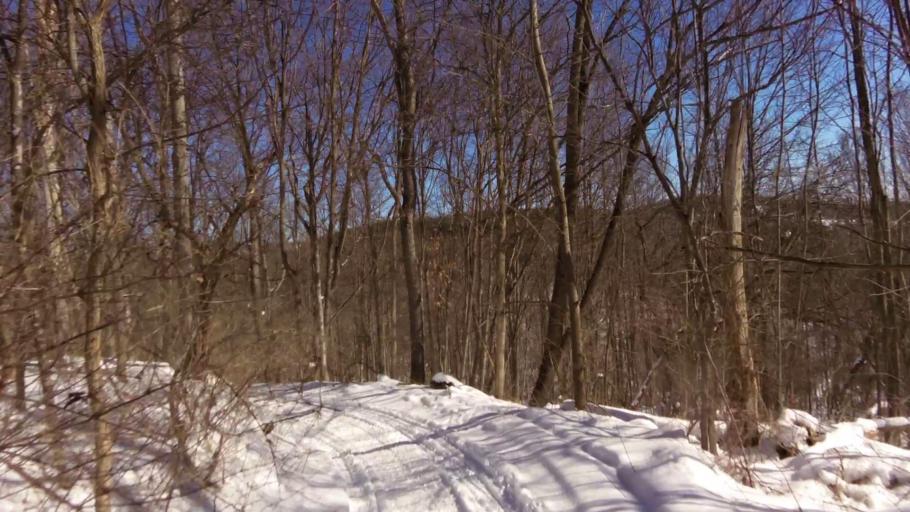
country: US
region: New York
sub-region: Allegany County
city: Cuba
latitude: 42.2791
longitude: -78.2304
